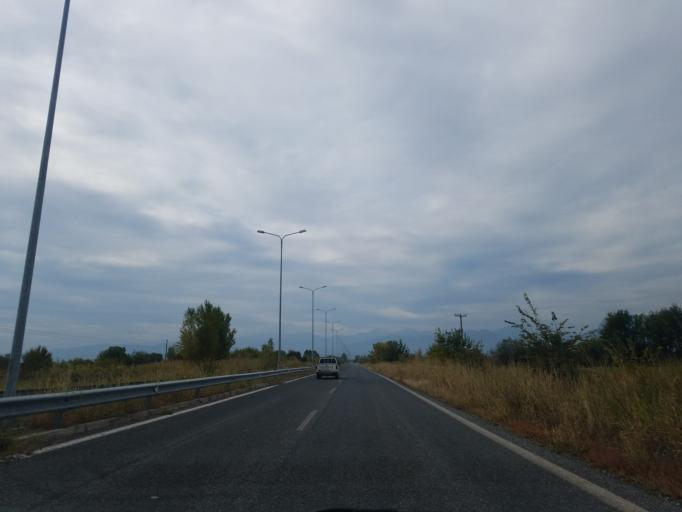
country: GR
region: Thessaly
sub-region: Trikala
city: Pyrgetos
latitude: 39.5650
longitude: 21.7381
